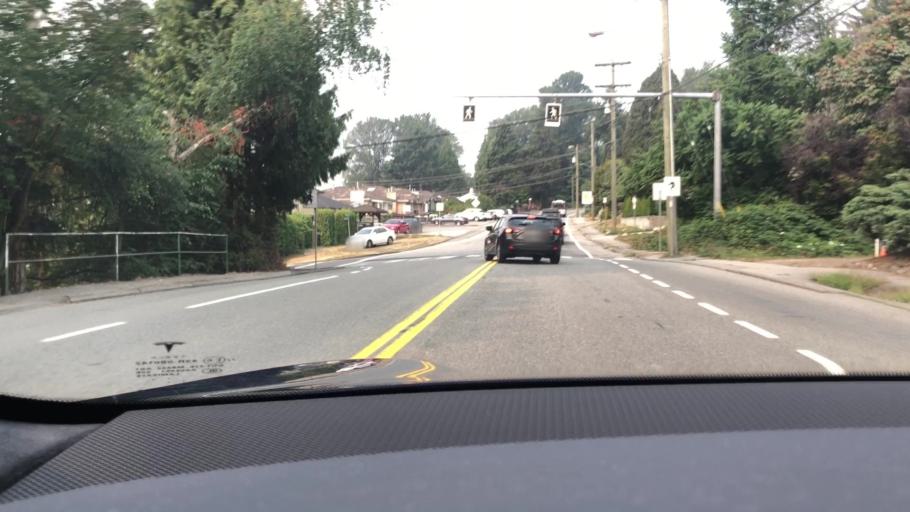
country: CA
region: British Columbia
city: Burnaby
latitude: 49.2084
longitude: -123.0174
